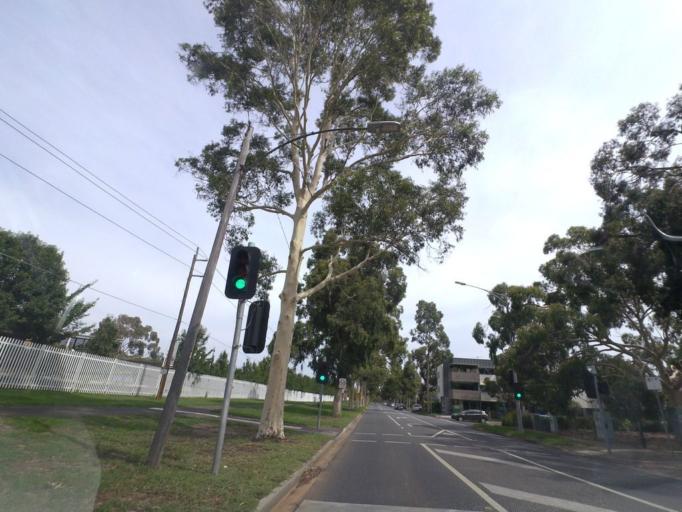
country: AU
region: Victoria
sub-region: Moonee Valley
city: Travancore
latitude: -37.7791
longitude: 144.9425
